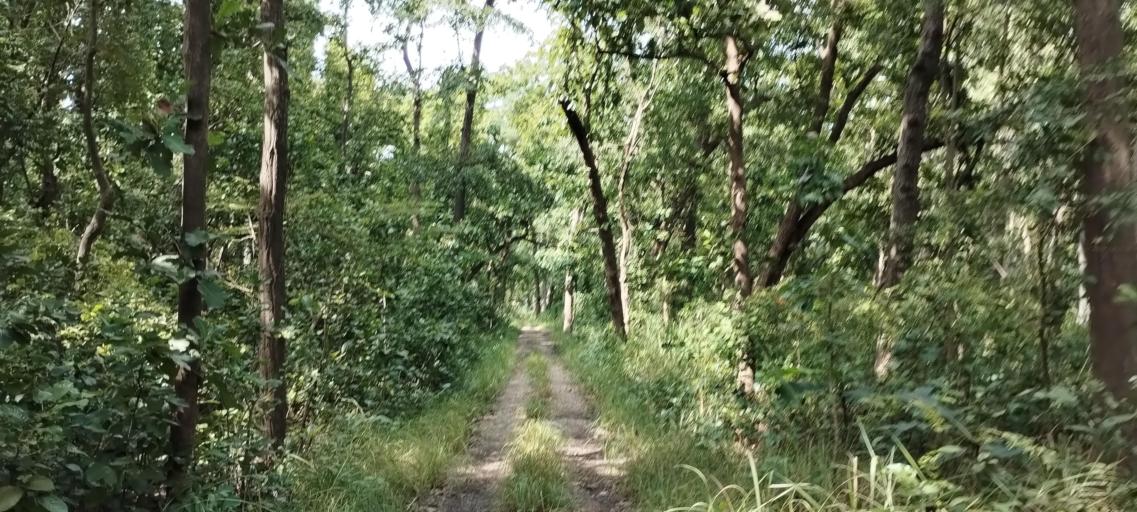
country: NP
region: Far Western
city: Tikapur
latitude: 28.5401
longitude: 81.2864
